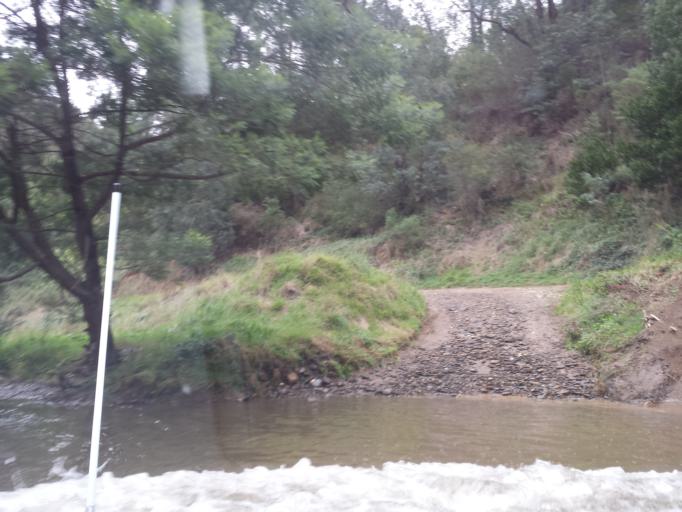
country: AU
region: Victoria
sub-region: Latrobe
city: Traralgon
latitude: -37.9984
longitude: 146.4726
